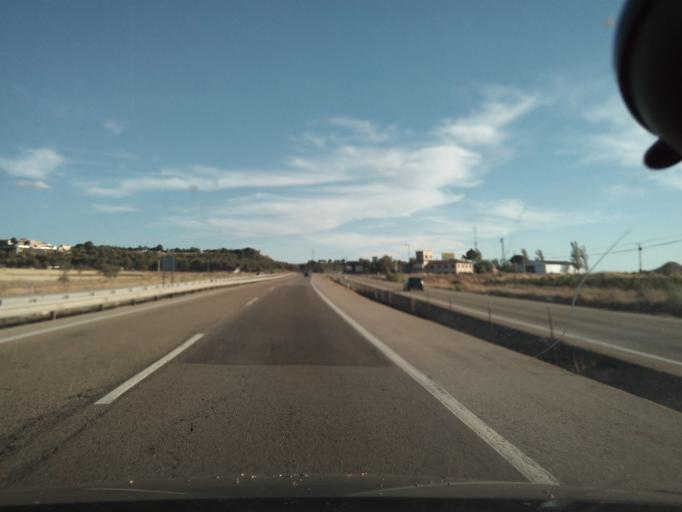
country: ES
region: Castille-La Mancha
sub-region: Province of Toledo
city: Dosbarrios
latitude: 39.7987
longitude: -3.4797
